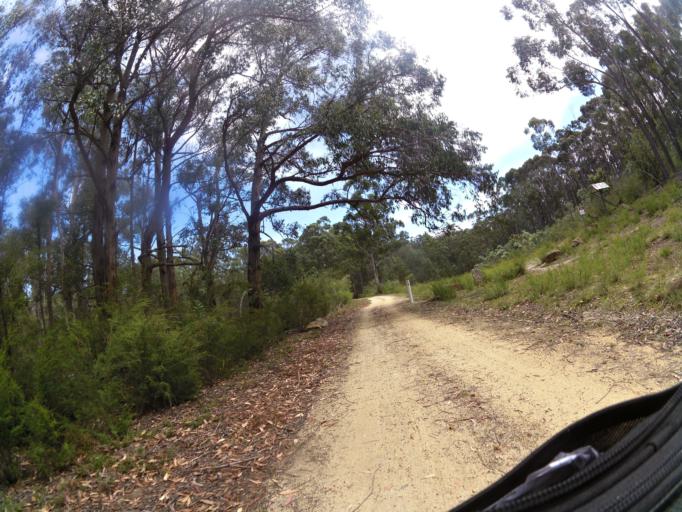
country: AU
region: Victoria
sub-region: East Gippsland
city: Lakes Entrance
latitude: -37.7398
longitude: 148.0190
